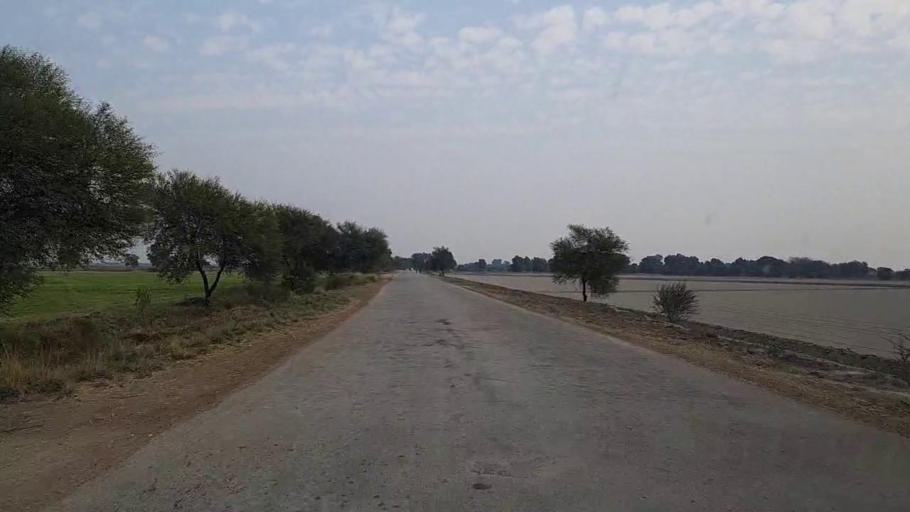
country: PK
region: Sindh
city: Mirwah Gorchani
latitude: 25.3951
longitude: 69.0712
